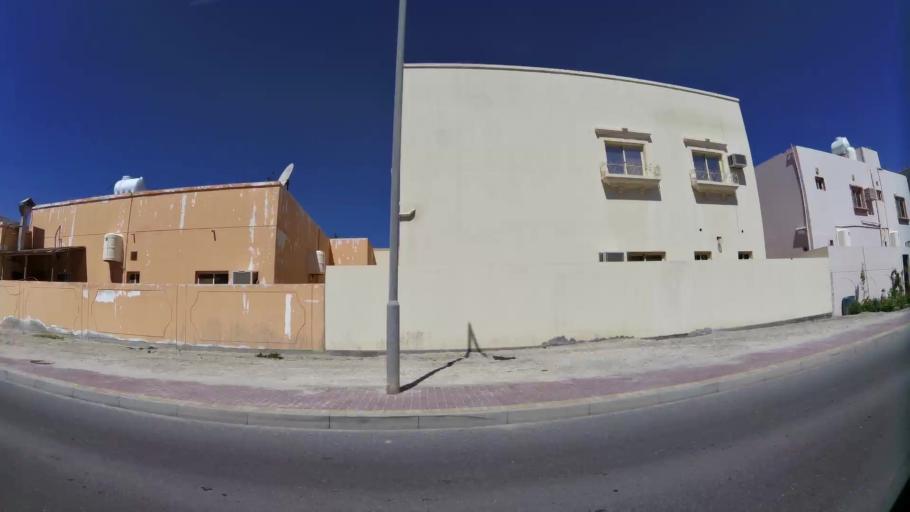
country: BH
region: Muharraq
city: Al Hadd
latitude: 26.2759
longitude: 50.6516
